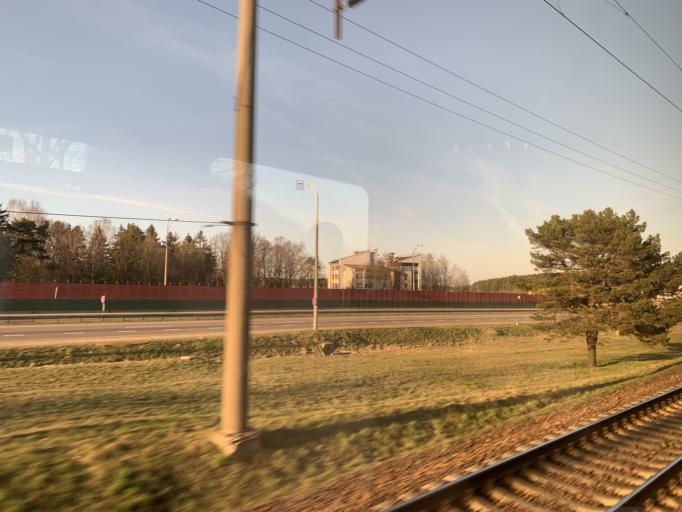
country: BY
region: Minsk
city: Zhdanovichy
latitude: 53.9521
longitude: 27.4047
